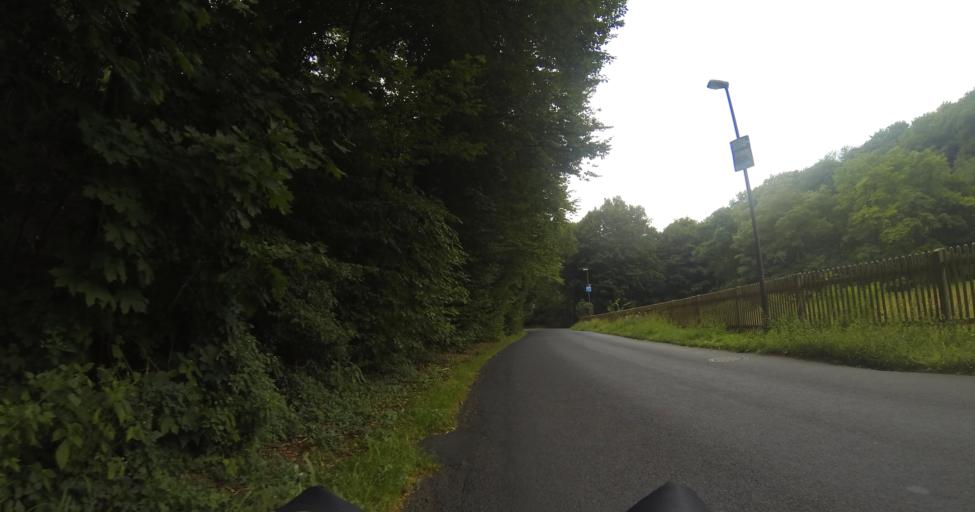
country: DE
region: Saxony
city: Radebeul
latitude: 51.1196
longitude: 13.6552
